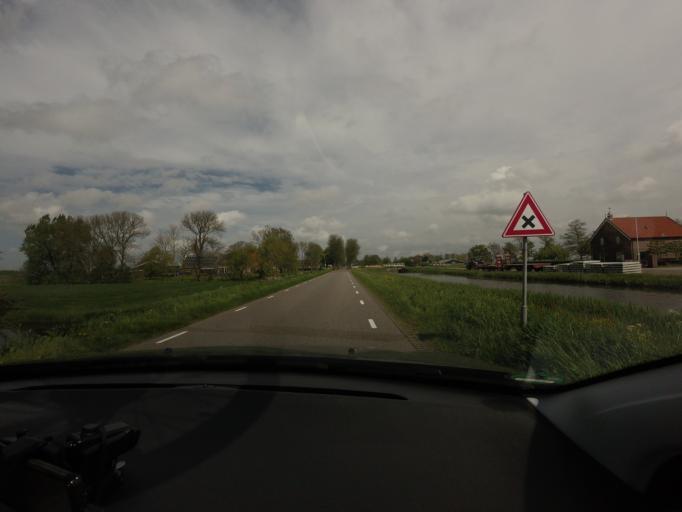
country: NL
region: North Holland
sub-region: Gemeente Alkmaar
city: Alkmaar
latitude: 52.5809
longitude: 4.7771
